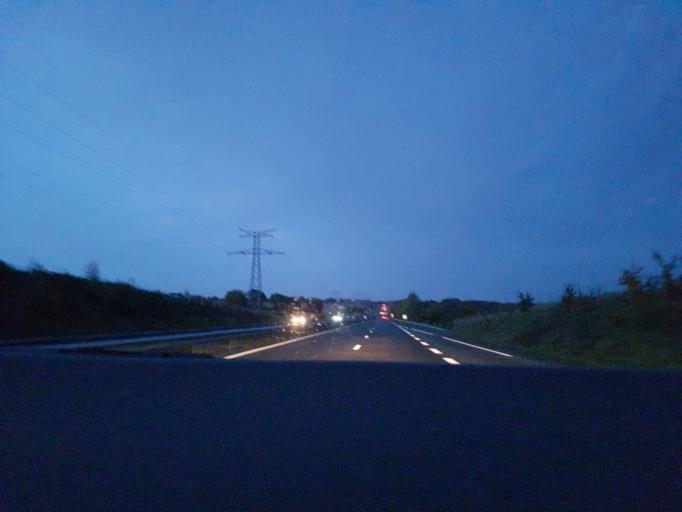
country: FR
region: Pays de la Loire
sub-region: Departement de la Mayenne
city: Louverne
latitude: 48.1335
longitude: -0.7121
